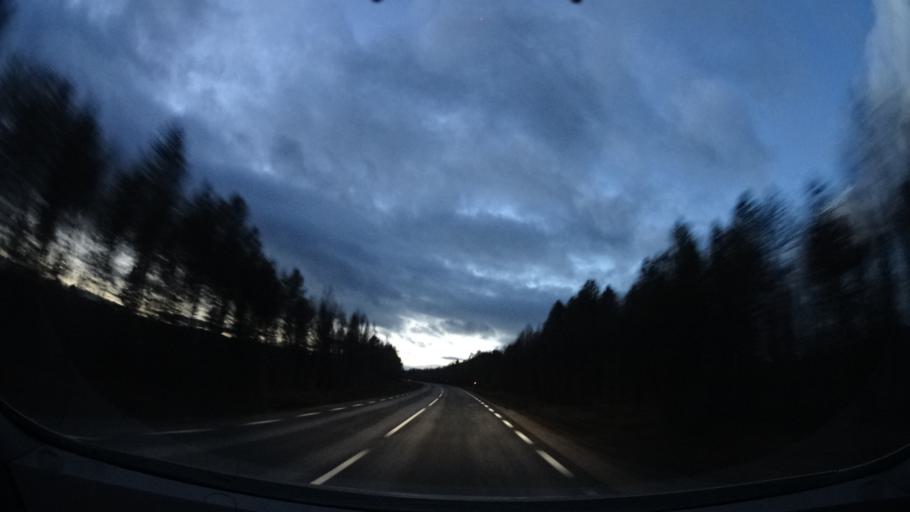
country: SE
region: Vaesterbotten
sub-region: Dorotea Kommun
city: Dorotea
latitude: 64.2405
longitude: 16.7368
